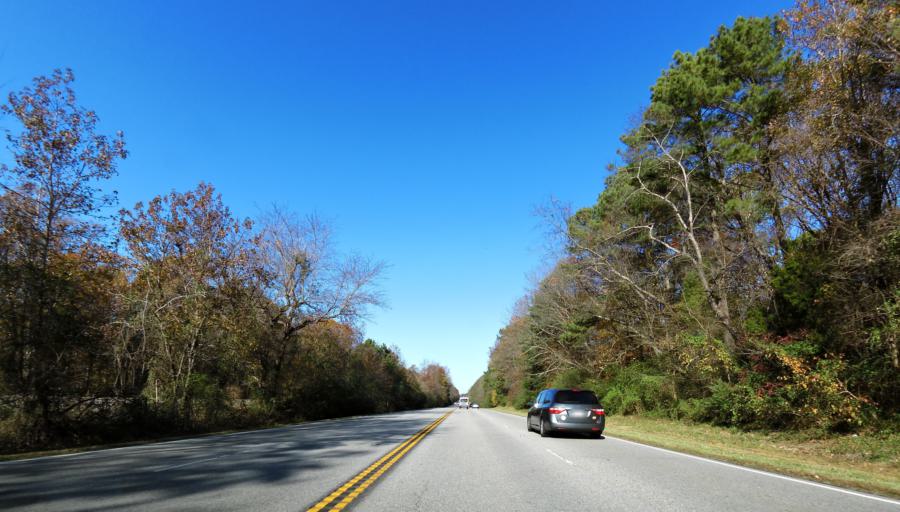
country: US
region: Virginia
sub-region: City of Williamsburg
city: Williamsburg
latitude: 37.2246
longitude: -76.6158
